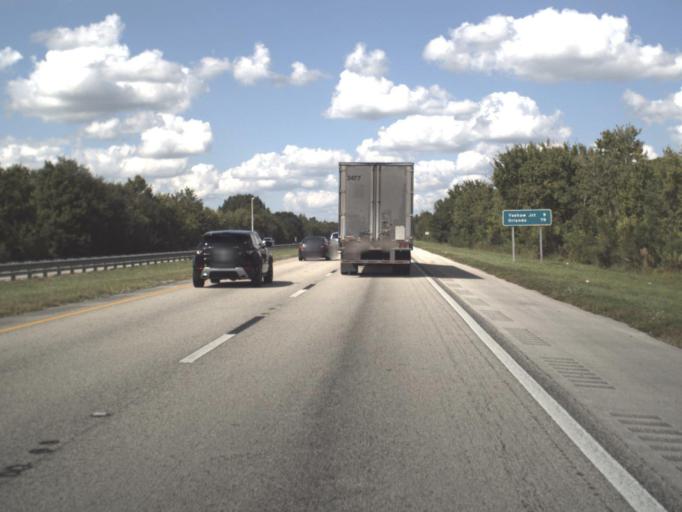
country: US
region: Florida
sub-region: Indian River County
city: Fellsmere
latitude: 27.6097
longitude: -80.8286
